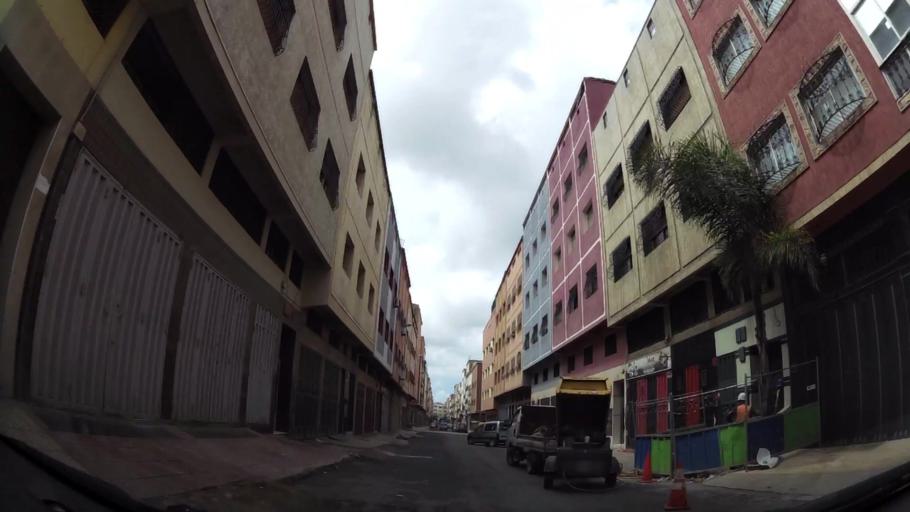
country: MA
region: Grand Casablanca
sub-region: Casablanca
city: Casablanca
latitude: 33.5342
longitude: -7.5905
